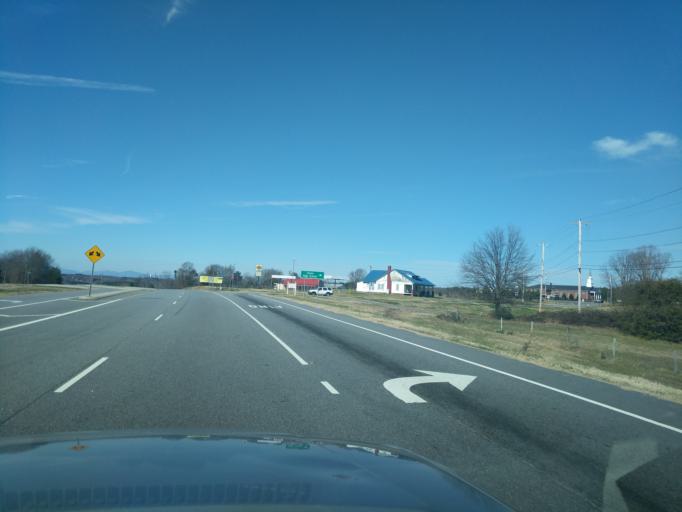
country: US
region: North Carolina
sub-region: Rutherford County
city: Forest City
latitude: 35.2362
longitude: -81.8478
